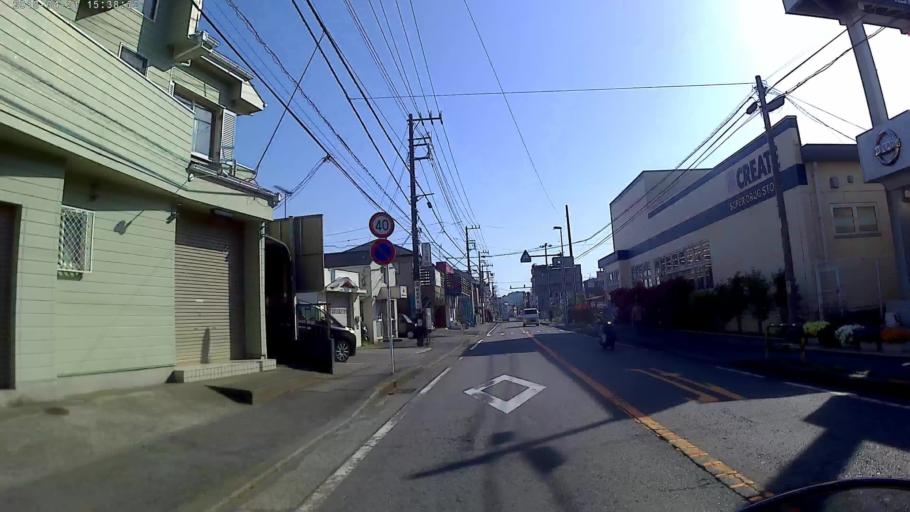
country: JP
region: Kanagawa
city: Fujisawa
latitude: 35.3160
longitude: 139.5028
